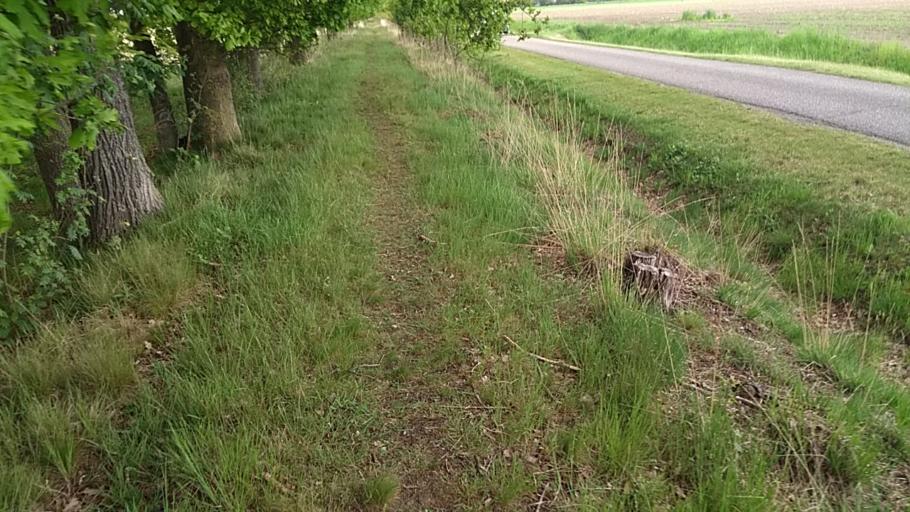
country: NL
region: Limburg
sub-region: Gemeente Leudal
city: Kelpen-Oler
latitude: 51.2757
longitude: 5.8353
